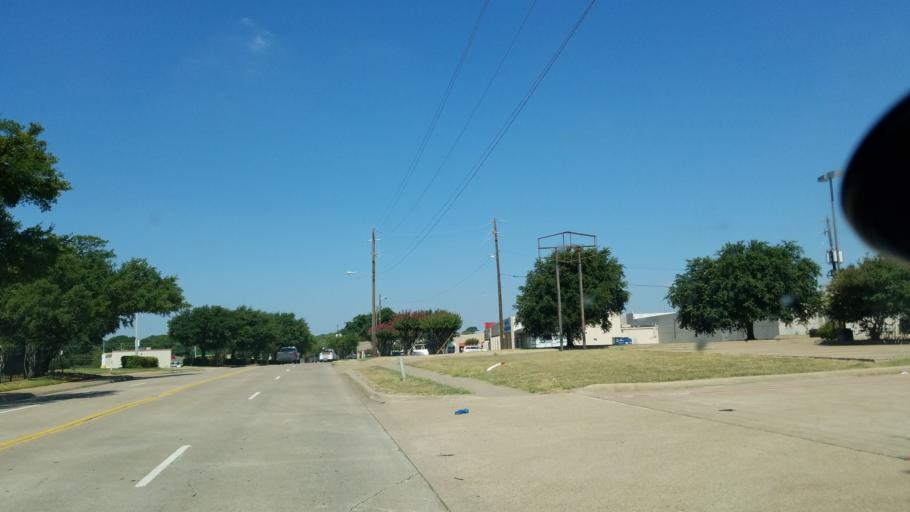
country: US
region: Texas
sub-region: Dallas County
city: Duncanville
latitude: 32.6561
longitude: -96.8885
